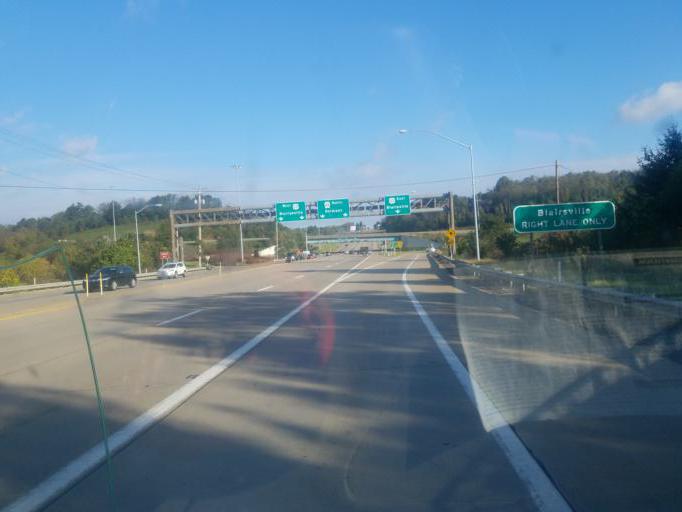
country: US
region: Pennsylvania
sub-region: Westmoreland County
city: Delmont
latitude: 40.3956
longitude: -79.5708
